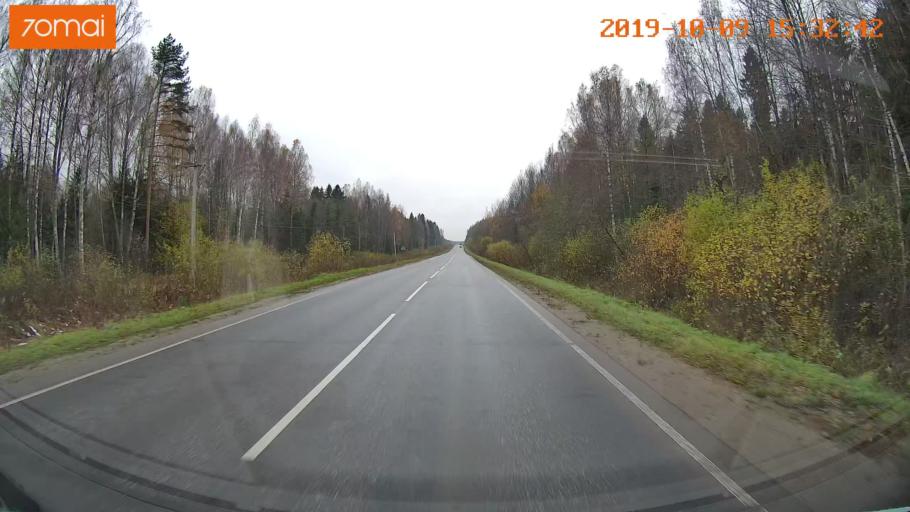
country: RU
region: Kostroma
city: Oktyabr'skiy
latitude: 57.9617
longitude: 41.2723
